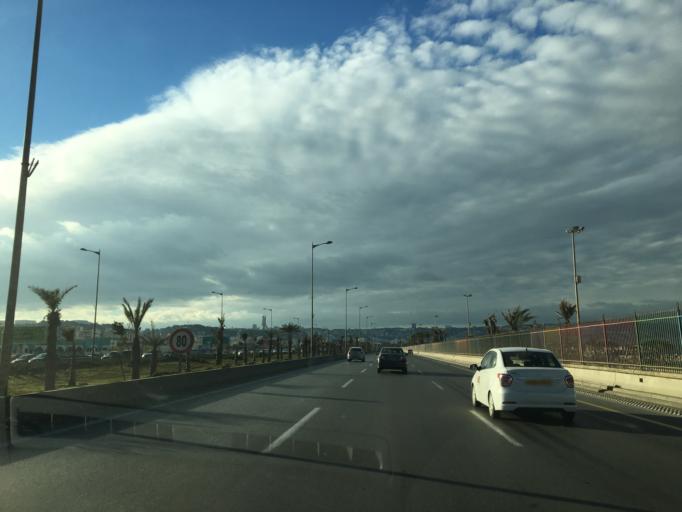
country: DZ
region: Alger
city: Birkhadem
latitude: 36.7434
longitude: 3.1113
